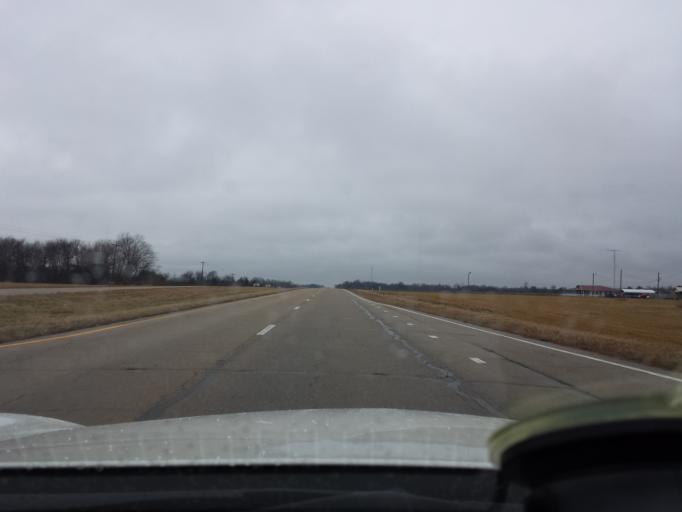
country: US
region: Mississippi
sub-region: Chickasaw County
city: Okolona
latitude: 33.8751
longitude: -88.7220
